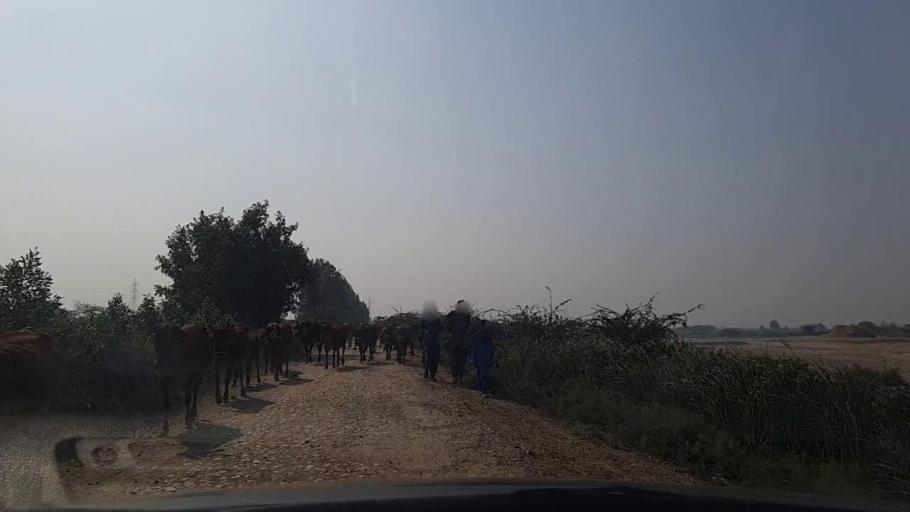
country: PK
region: Sindh
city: Mirpur Sakro
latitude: 24.5728
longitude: 67.7799
